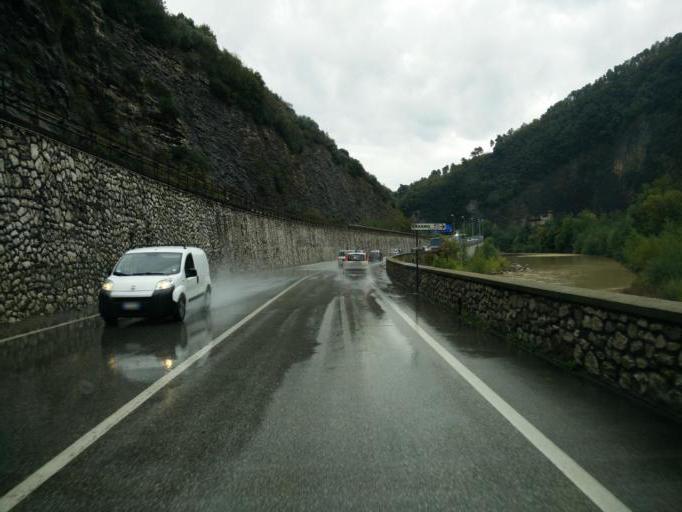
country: IT
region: Tuscany
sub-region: Provincia di Lucca
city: Valdottavo
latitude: 43.9290
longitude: 10.5150
